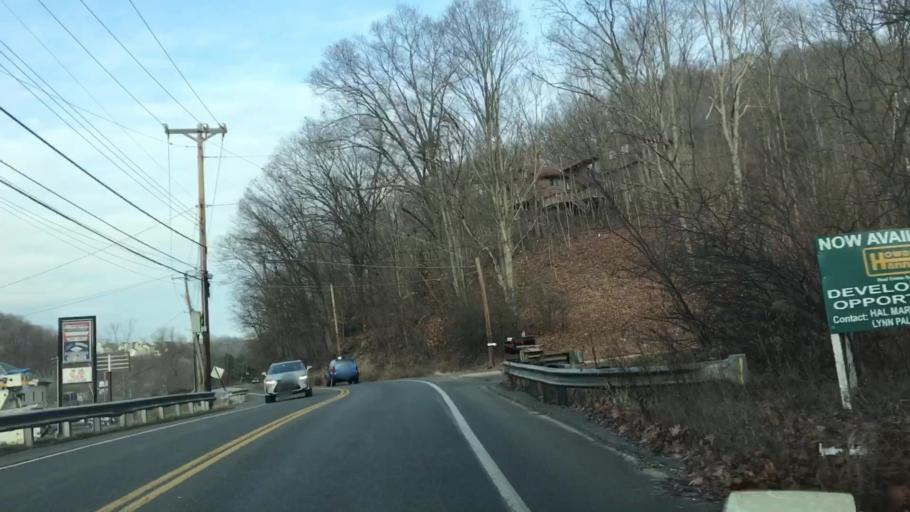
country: US
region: Pennsylvania
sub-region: Allegheny County
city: Ben Avon
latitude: 40.5374
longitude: -80.0753
